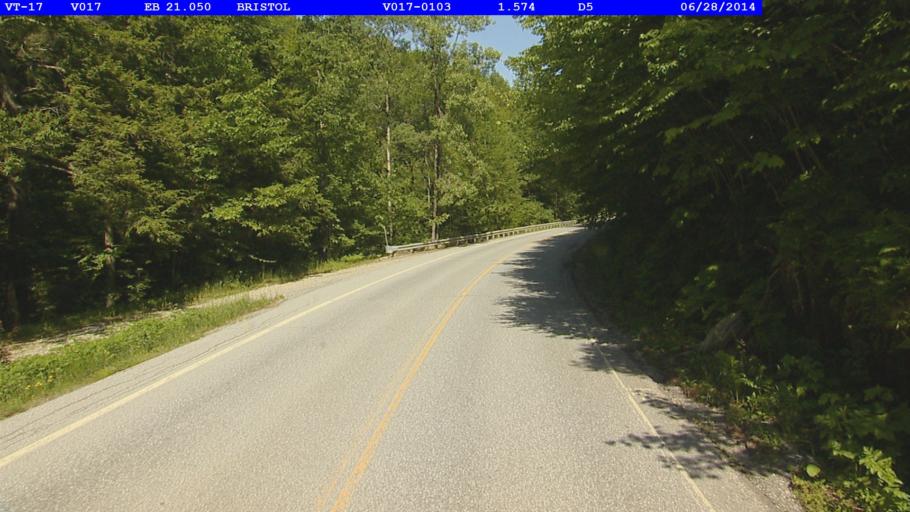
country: US
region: Vermont
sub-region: Addison County
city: Bristol
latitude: 44.1612
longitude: -73.0315
